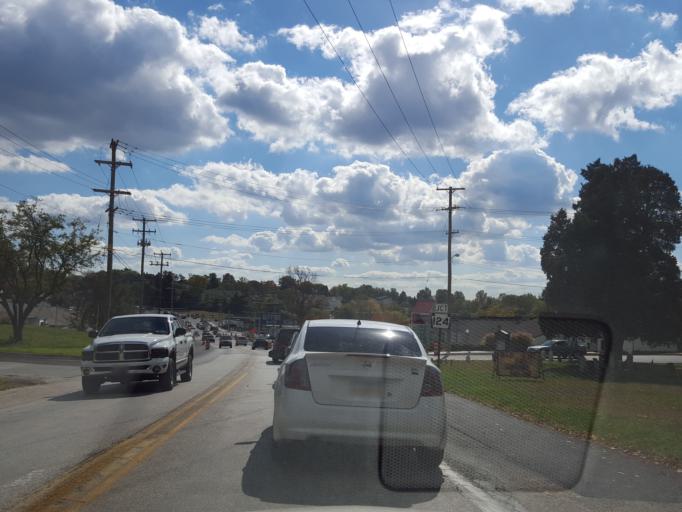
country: US
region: Pennsylvania
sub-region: York County
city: East York
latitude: 39.9617
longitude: -76.6604
